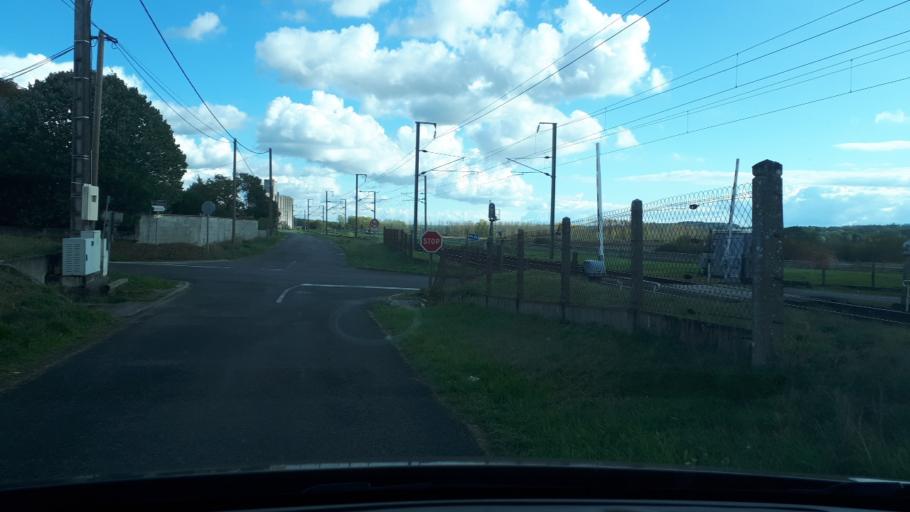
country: FR
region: Centre
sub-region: Departement du Loir-et-Cher
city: Mareuil-sur-Cher
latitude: 47.3009
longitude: 1.3541
